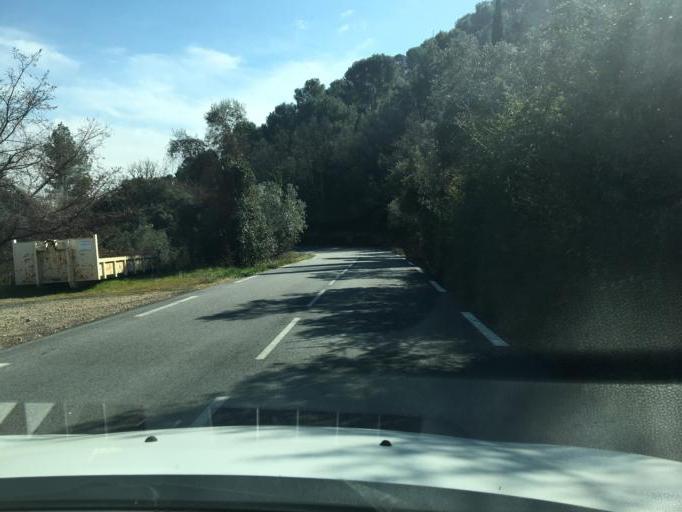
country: FR
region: Provence-Alpes-Cote d'Azur
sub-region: Departement du Var
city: Bargemon
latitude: 43.6133
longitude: 6.5460
